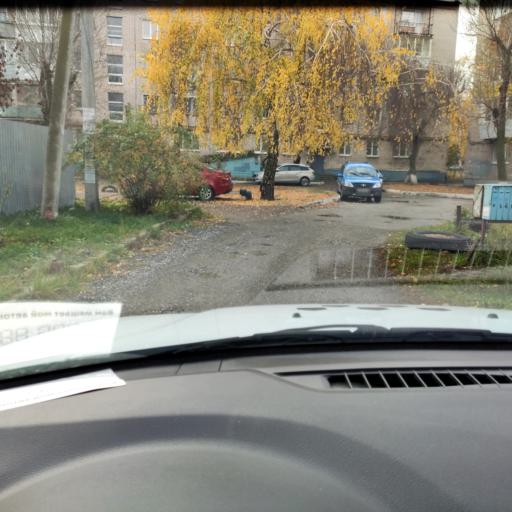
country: RU
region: Samara
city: Tol'yatti
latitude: 53.5303
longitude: 49.4013
